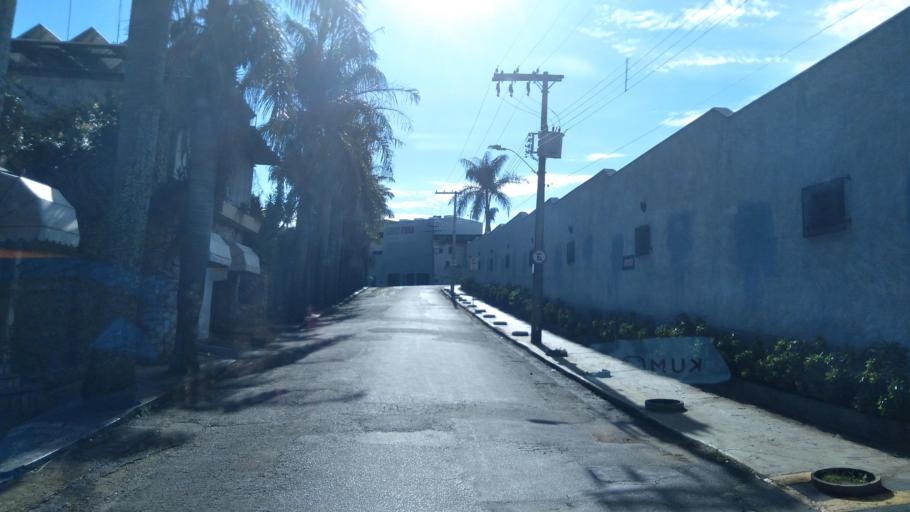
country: BR
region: Minas Gerais
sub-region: Contagem
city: Contagem
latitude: -19.9257
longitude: -44.0083
